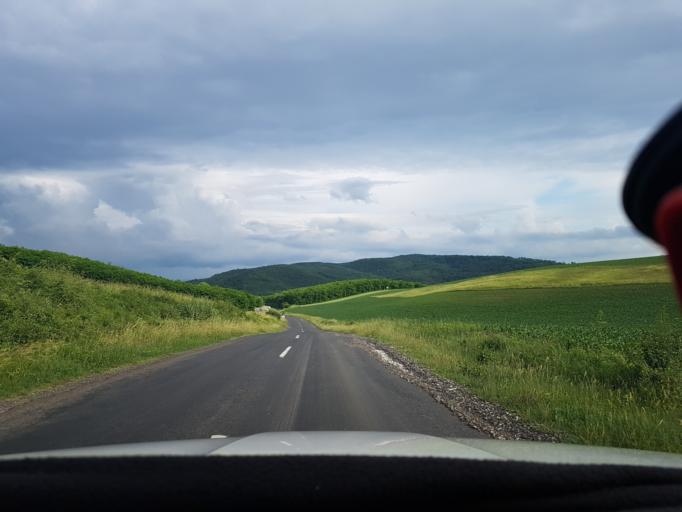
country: HU
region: Komarom-Esztergom
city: Nyergesujfalu
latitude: 47.7211
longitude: 18.5505
